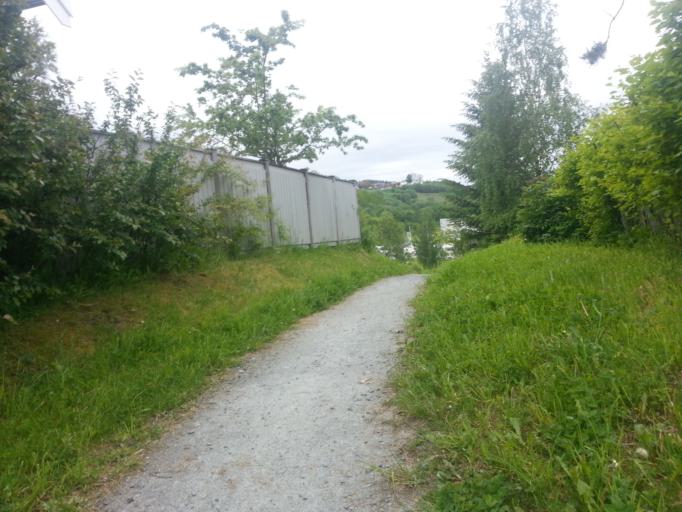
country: NO
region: Sor-Trondelag
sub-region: Trondheim
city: Trondheim
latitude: 63.4078
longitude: 10.4458
